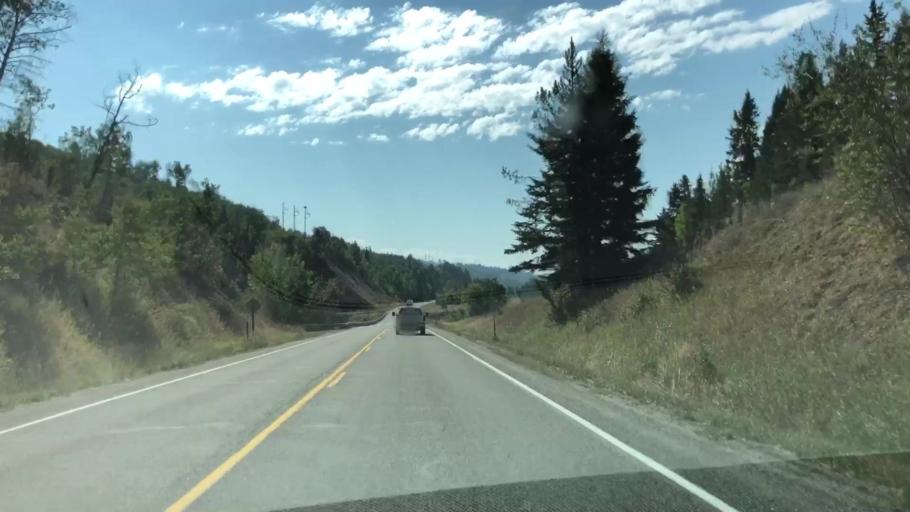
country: US
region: Idaho
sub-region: Teton County
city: Victor
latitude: 43.2955
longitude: -111.1273
